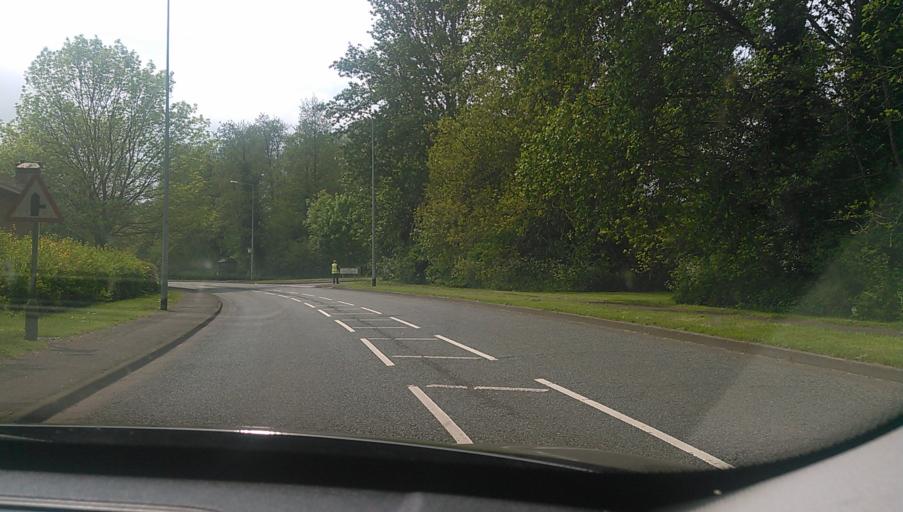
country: GB
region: England
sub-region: Shropshire
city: Hadley
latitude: 52.7161
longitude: -2.4967
